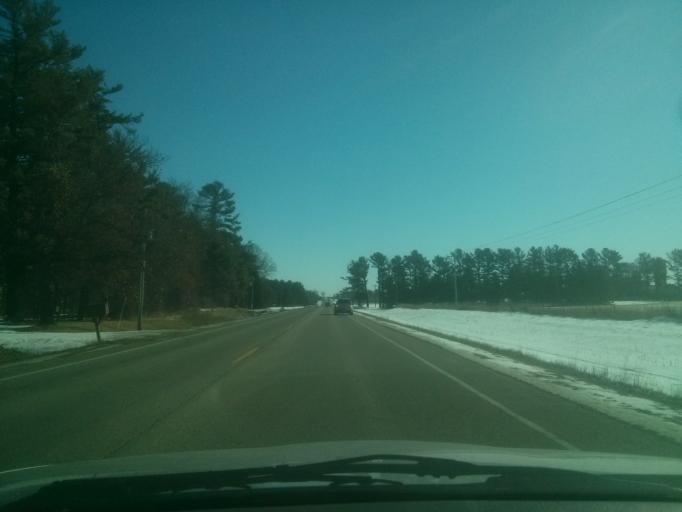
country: US
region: Wisconsin
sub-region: Saint Croix County
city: New Richmond
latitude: 45.1366
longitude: -92.4002
